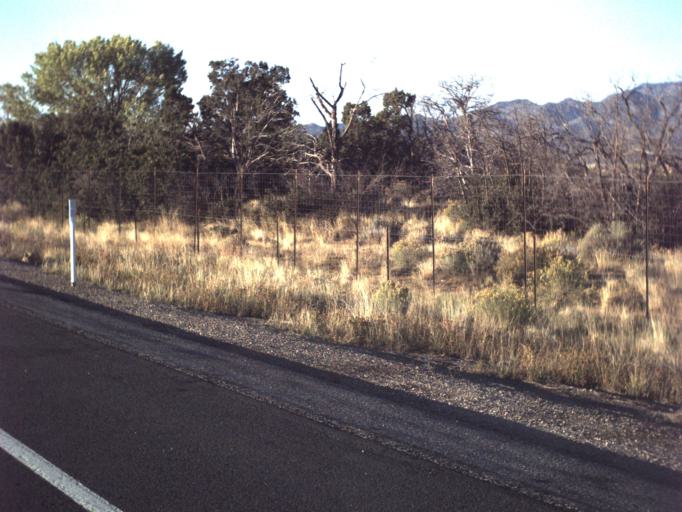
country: US
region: Utah
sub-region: Iron County
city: Cedar City
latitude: 37.5138
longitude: -113.2126
